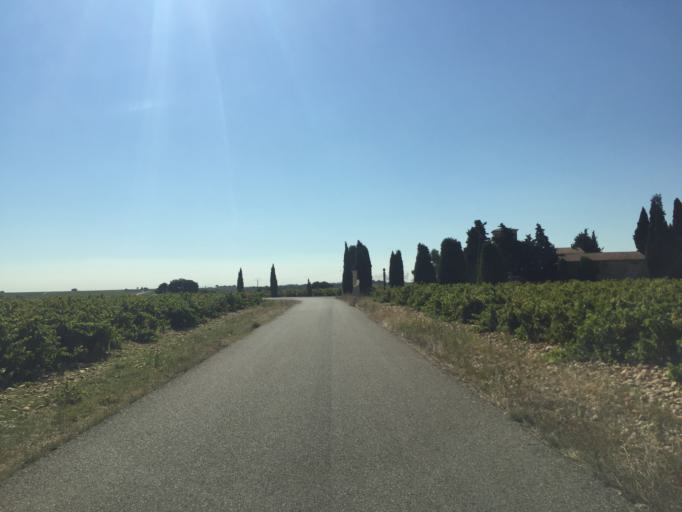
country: FR
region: Provence-Alpes-Cote d'Azur
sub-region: Departement du Vaucluse
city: Chateauneuf-du-Pape
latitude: 44.0824
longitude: 4.8273
